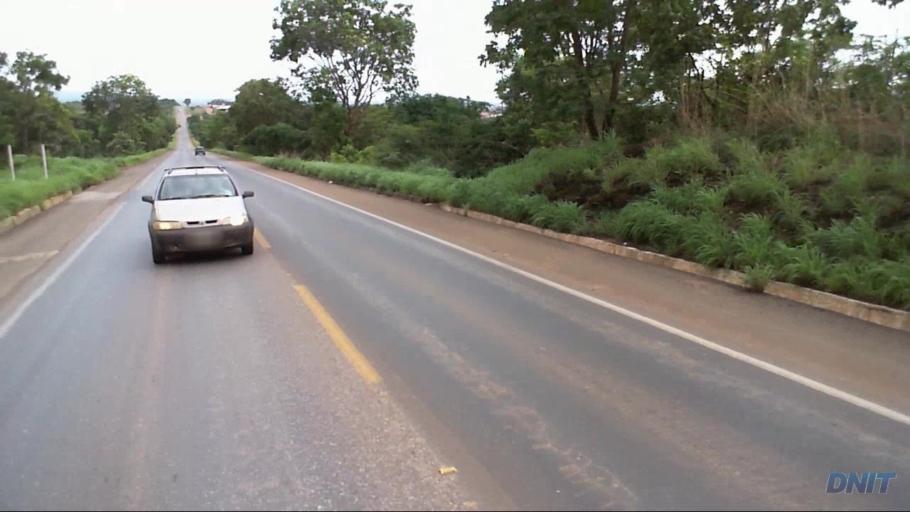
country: BR
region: Goias
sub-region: Uruacu
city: Uruacu
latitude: -14.5573
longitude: -49.1580
